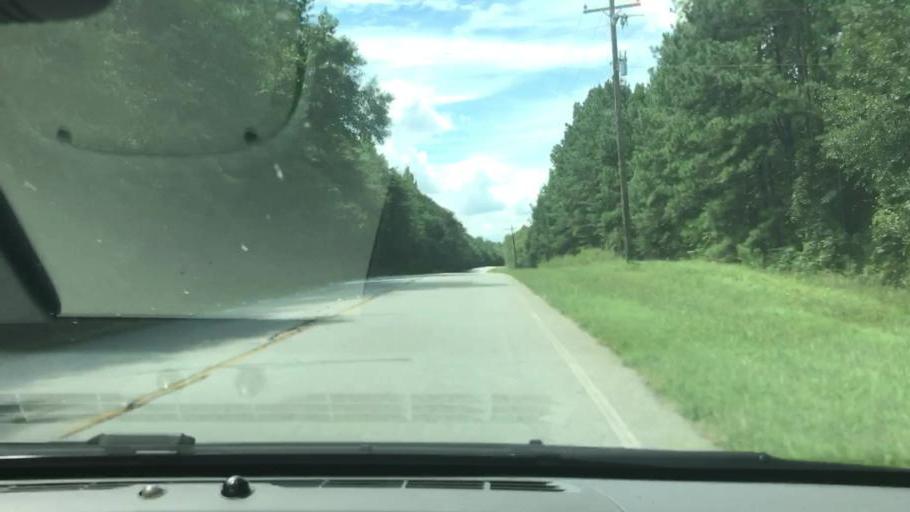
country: US
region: Georgia
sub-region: Stewart County
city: Lumpkin
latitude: 32.1390
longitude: -84.9417
